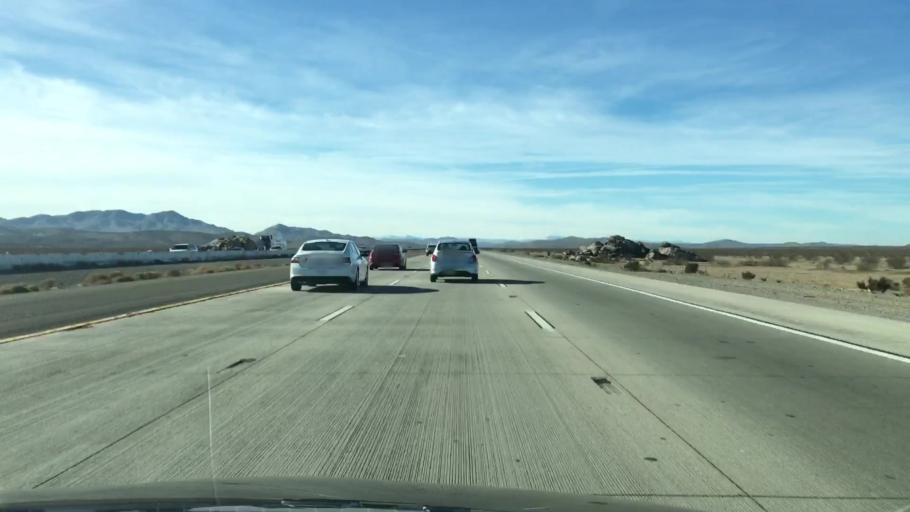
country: US
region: California
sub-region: San Bernardino County
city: Lenwood
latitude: 34.7880
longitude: -117.1237
